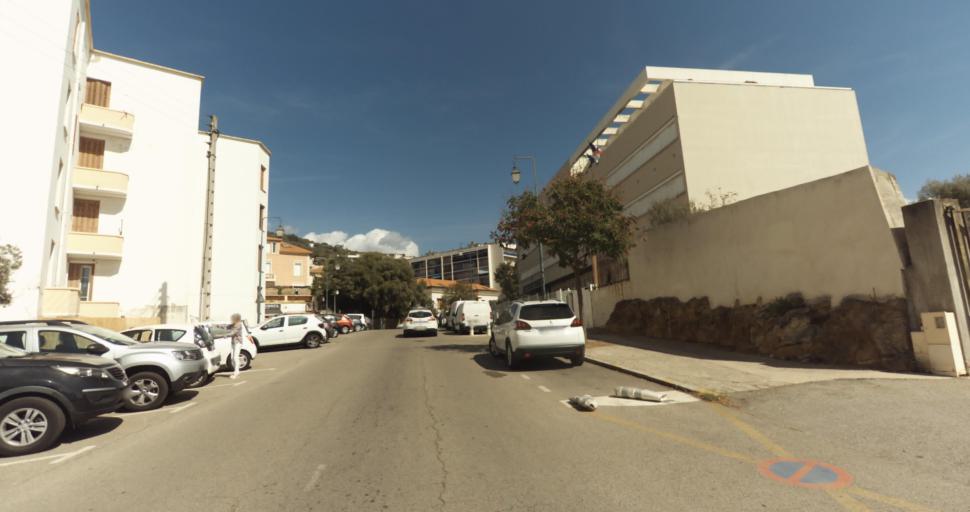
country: FR
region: Corsica
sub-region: Departement de la Corse-du-Sud
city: Ajaccio
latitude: 41.9144
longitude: 8.7266
